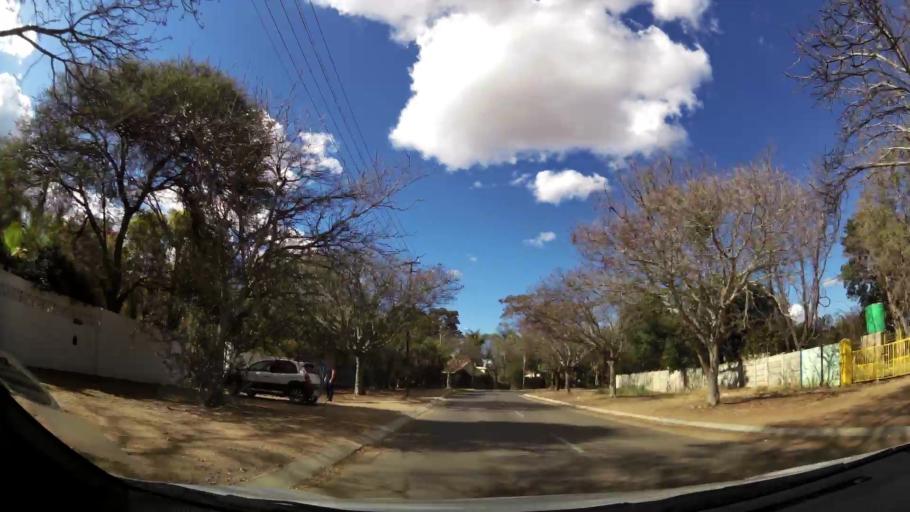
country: ZA
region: Limpopo
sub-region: Capricorn District Municipality
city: Polokwane
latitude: -23.8820
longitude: 29.4686
